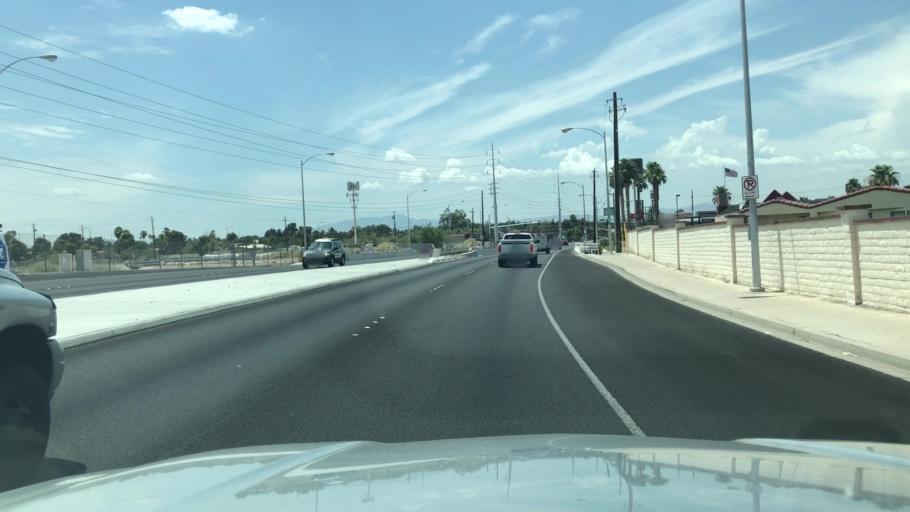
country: US
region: Nevada
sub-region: Clark County
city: Whitney
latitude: 36.0859
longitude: -115.0705
